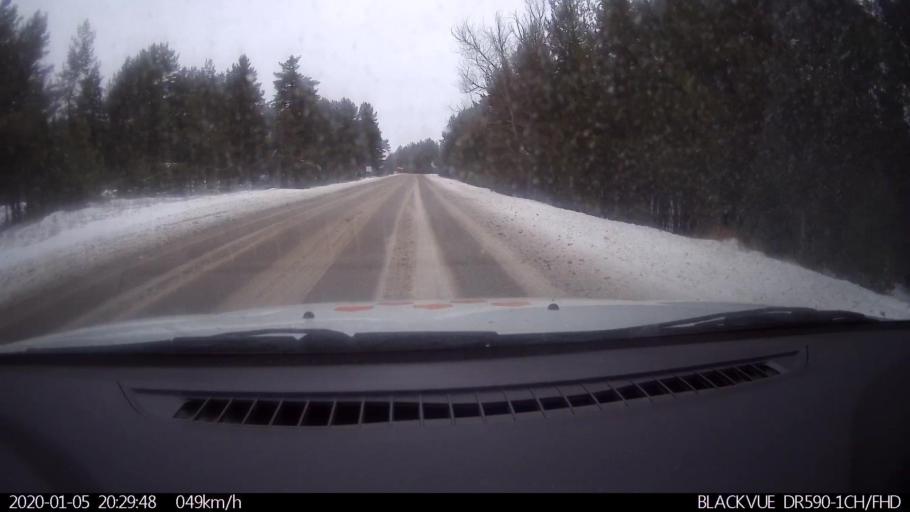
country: RU
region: Nizjnij Novgorod
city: Lukino
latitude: 56.3954
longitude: 43.7318
